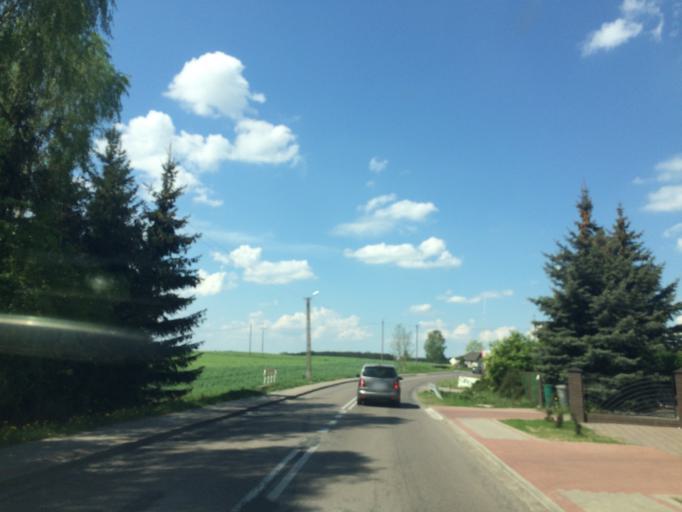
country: PL
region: Warmian-Masurian Voivodeship
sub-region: Powiat dzialdowski
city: Rybno
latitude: 53.3849
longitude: 19.9228
